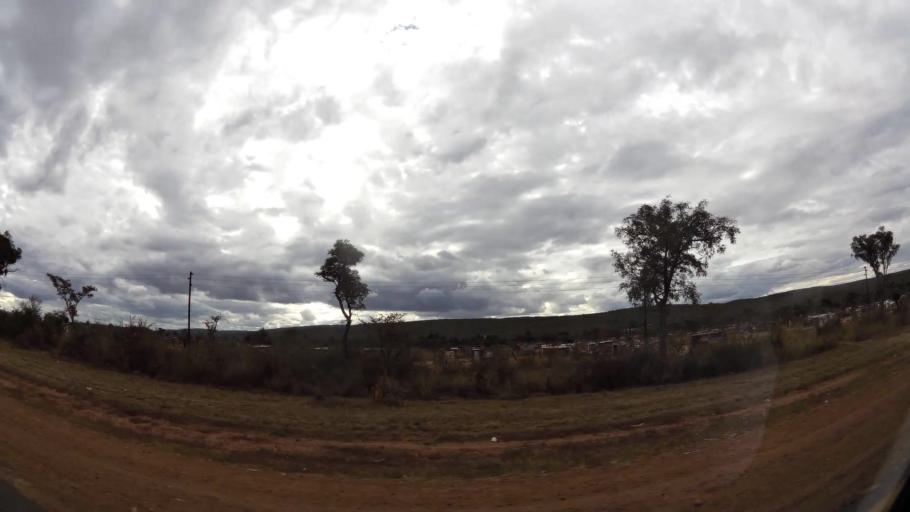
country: ZA
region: Limpopo
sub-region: Waterberg District Municipality
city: Modimolle
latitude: -24.6817
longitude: 28.4318
